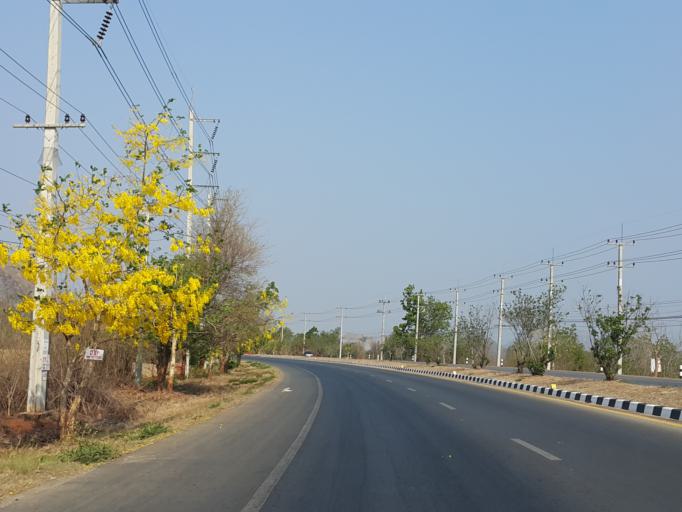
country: TH
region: Kanchanaburi
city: Kanchanaburi
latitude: 14.0687
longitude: 99.4064
